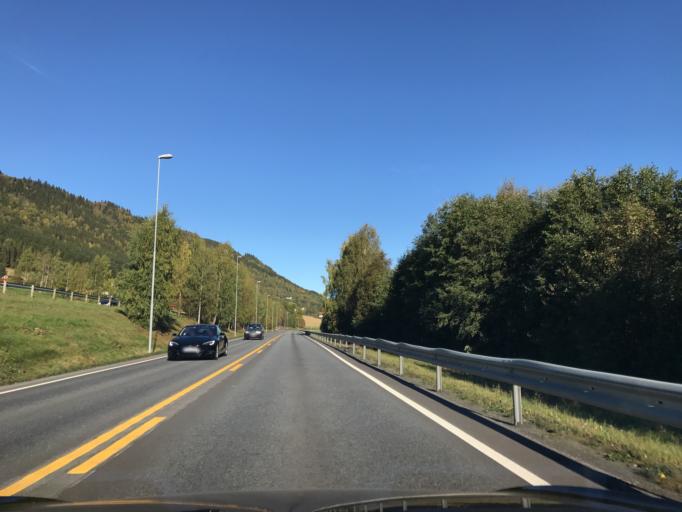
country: NO
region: Oppland
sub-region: Lillehammer
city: Lillehammer
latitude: 61.0750
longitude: 10.4313
